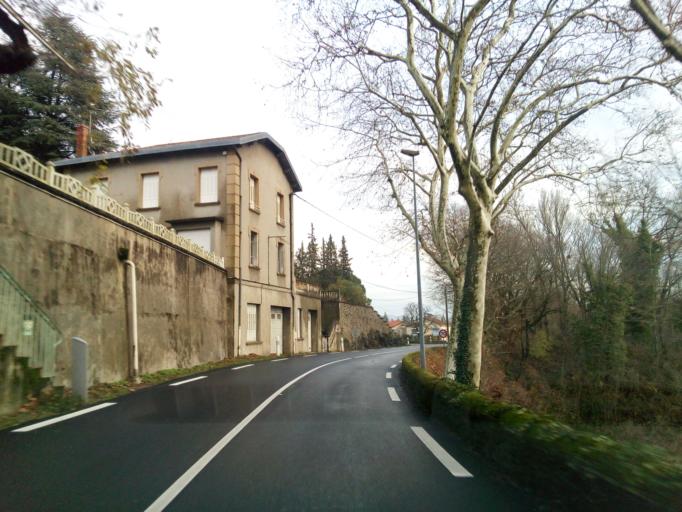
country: FR
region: Rhone-Alpes
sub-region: Departement de l'Ardeche
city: Beauchastel
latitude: 44.8282
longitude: 4.7871
